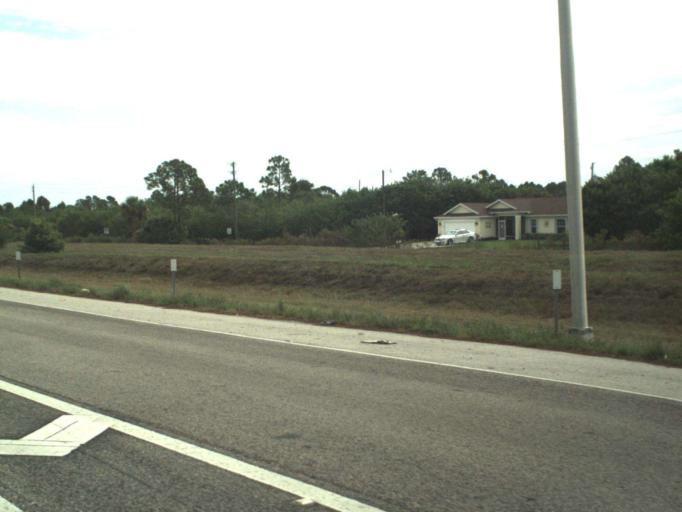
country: US
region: Florida
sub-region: Saint Lucie County
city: Port Saint Lucie
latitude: 27.2140
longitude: -80.4002
